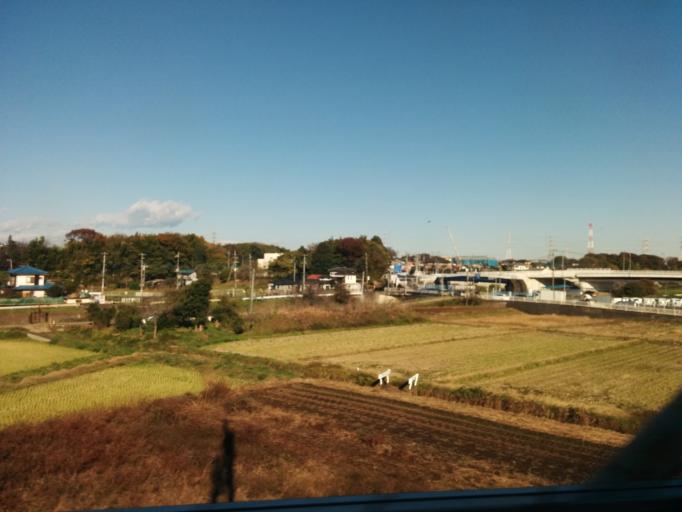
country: JP
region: Kanagawa
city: Atsugi
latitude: 35.4060
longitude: 139.4070
